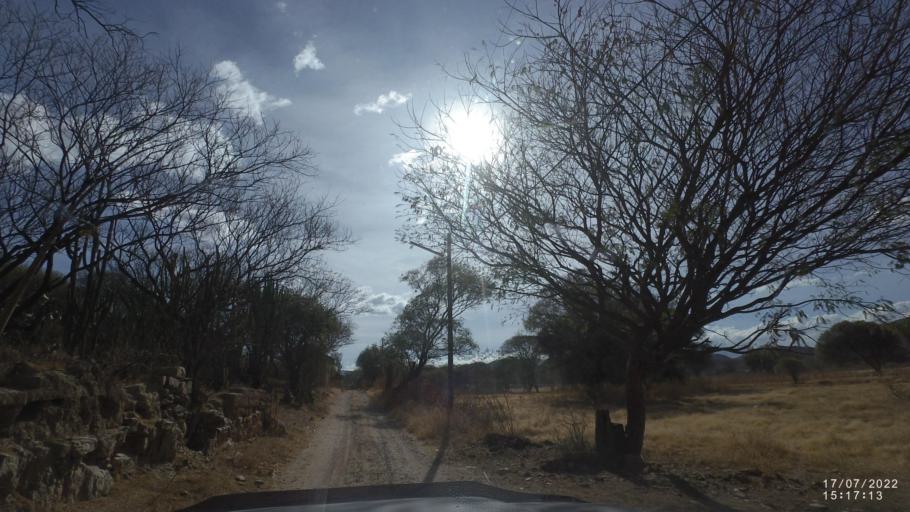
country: BO
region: Cochabamba
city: Sipe Sipe
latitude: -17.5517
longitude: -66.2666
